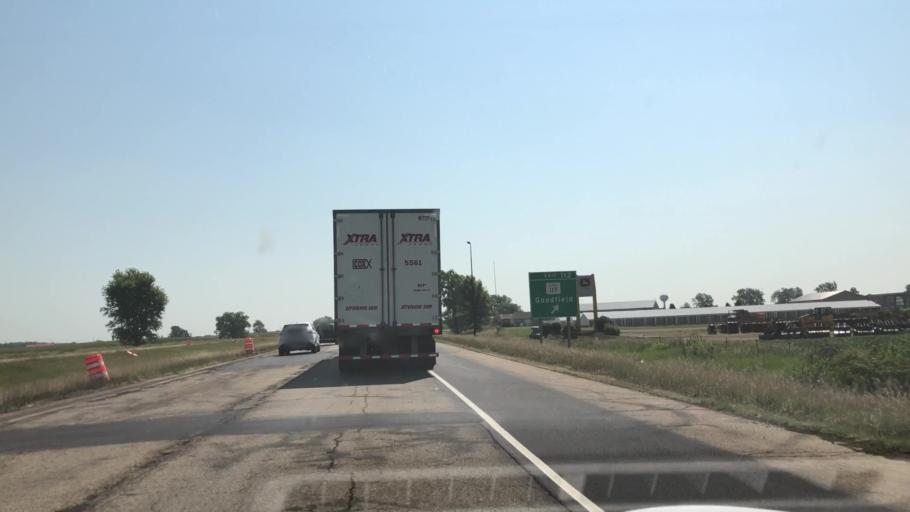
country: US
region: Illinois
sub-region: Woodford County
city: Eureka
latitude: 40.6224
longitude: -89.2820
